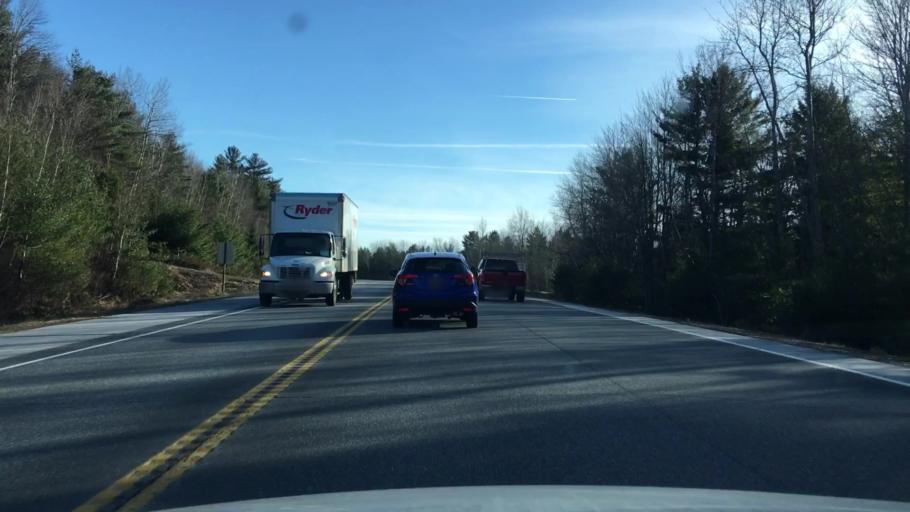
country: US
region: Maine
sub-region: Hancock County
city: Dedham
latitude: 44.6718
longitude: -68.5774
